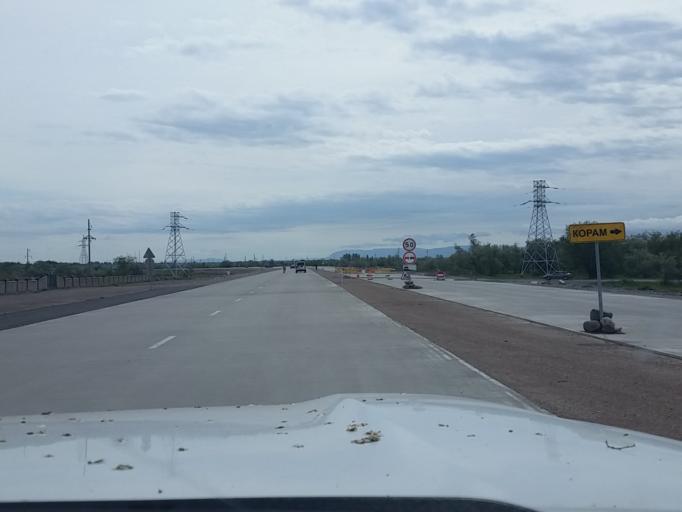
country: KZ
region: Almaty Oblysy
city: Turgen'
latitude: 43.5783
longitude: 78.1995
